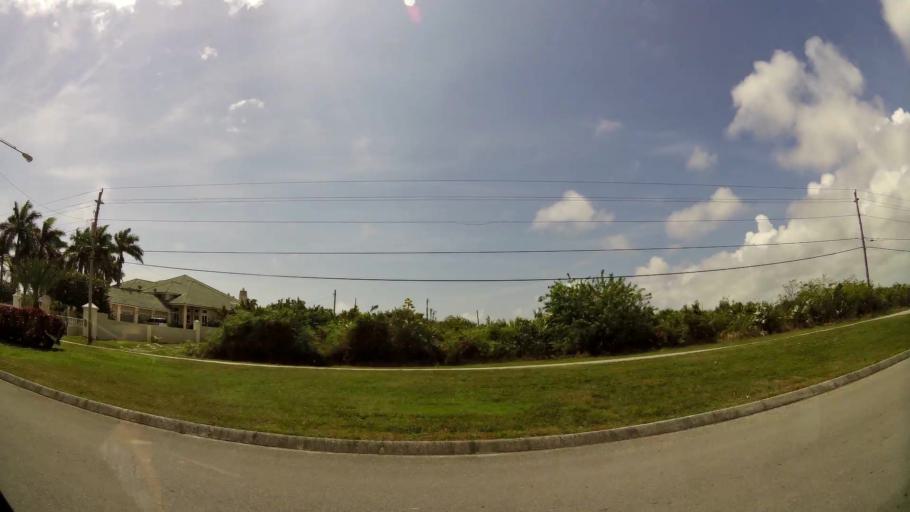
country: BS
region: Freeport
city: Freeport
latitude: 26.5078
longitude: -78.6979
